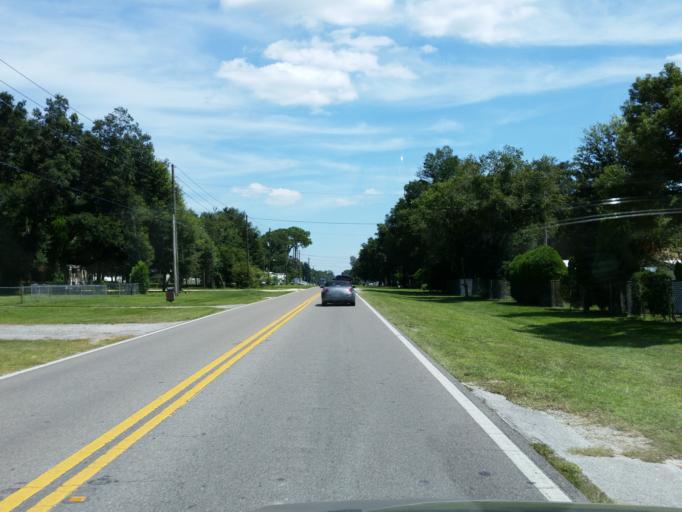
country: US
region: Florida
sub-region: Pasco County
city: Zephyrhills North
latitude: 28.2519
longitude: -82.1661
